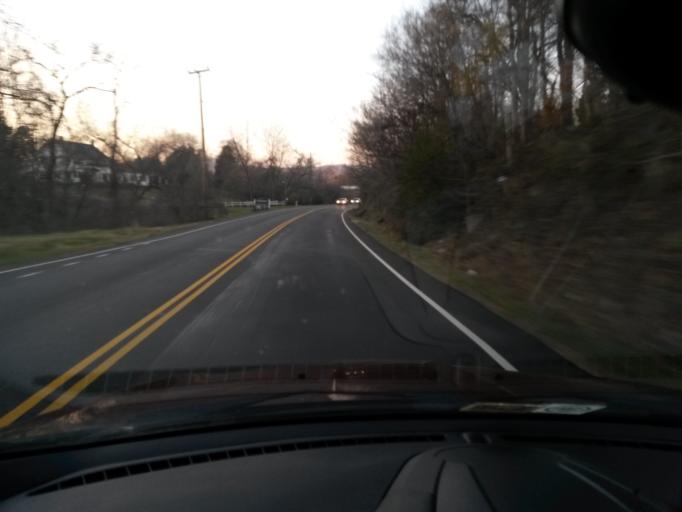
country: US
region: Virginia
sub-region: Roanoke County
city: Hollins
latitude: 37.3451
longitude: -79.9481
